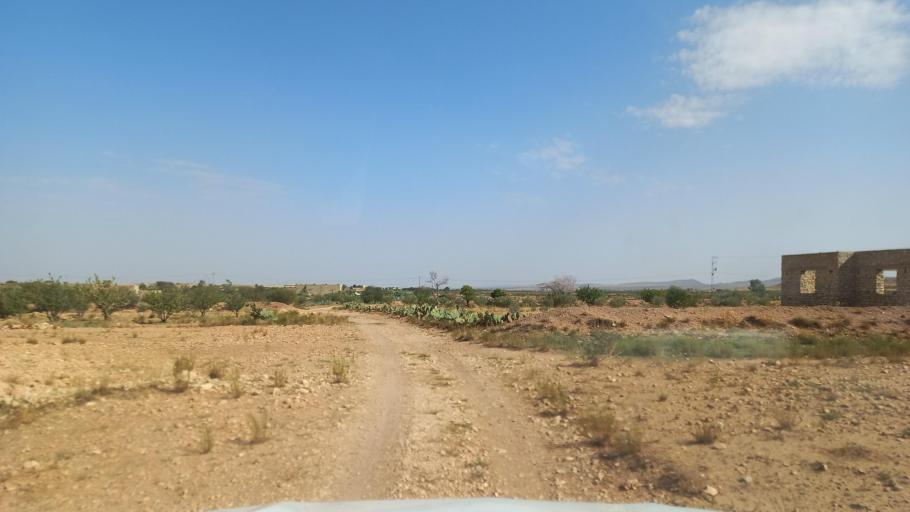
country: TN
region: Al Qasrayn
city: Kasserine
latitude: 35.2805
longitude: 8.9544
